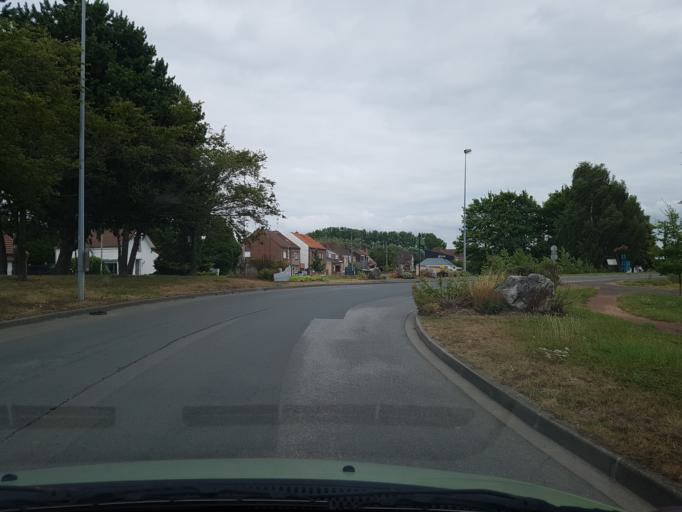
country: FR
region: Nord-Pas-de-Calais
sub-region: Departement du Nord
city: Bauvin
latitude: 50.5234
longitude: 2.8802
